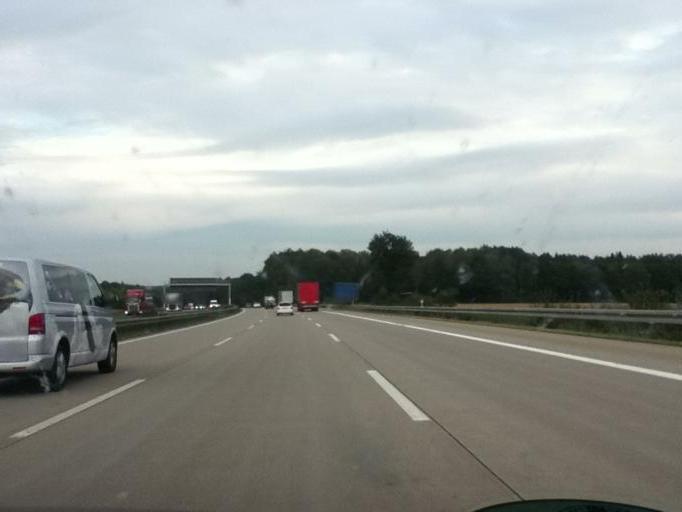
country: DE
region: Saxony
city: Rosswein
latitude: 51.0010
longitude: 13.2118
